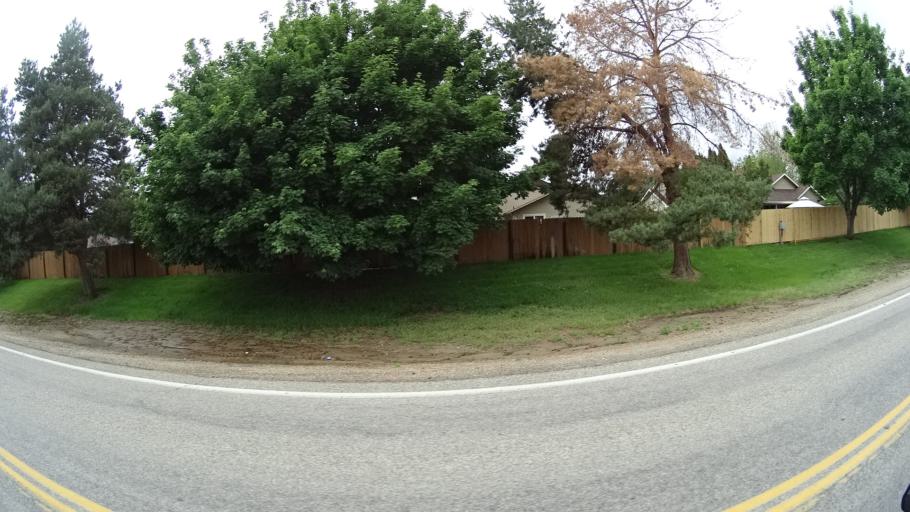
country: US
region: Idaho
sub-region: Ada County
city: Eagle
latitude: 43.7094
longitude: -116.3146
